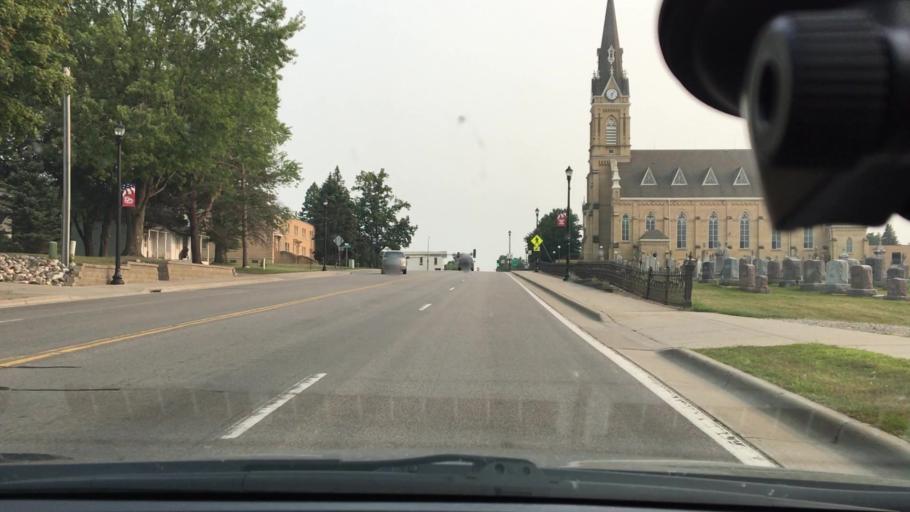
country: US
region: Minnesota
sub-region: Wright County
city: Saint Michael
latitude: 45.2121
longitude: -93.6648
